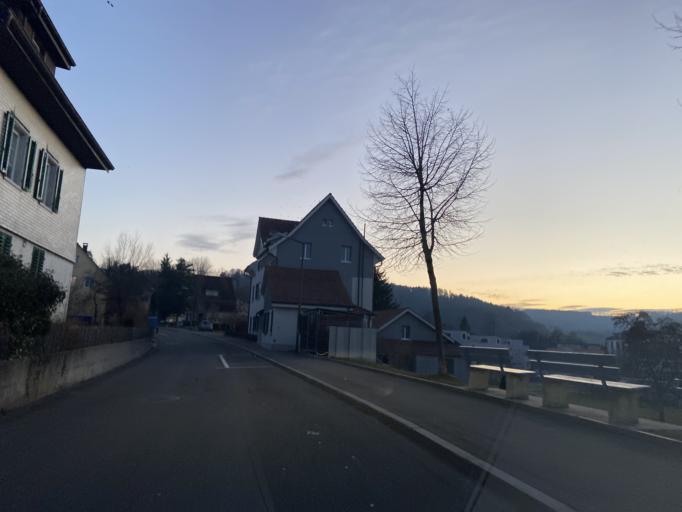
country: CH
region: Zurich
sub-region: Bezirk Winterthur
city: Wuelflingen (Kreis 6) / Lindenplatz
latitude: 47.5086
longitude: 8.6942
